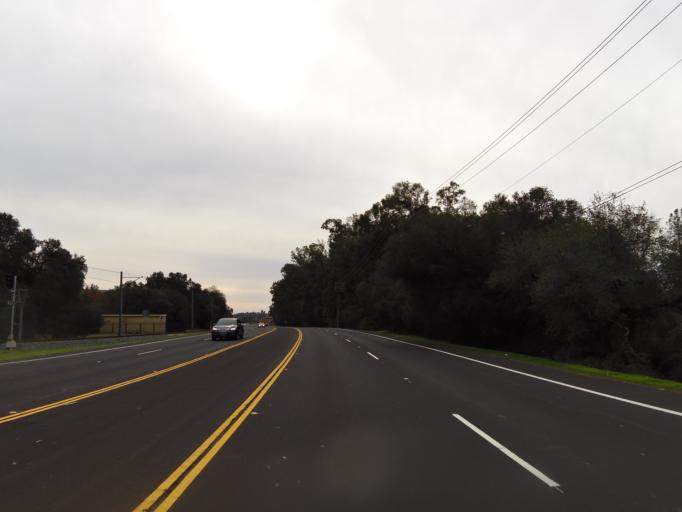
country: US
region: California
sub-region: Sacramento County
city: Folsom
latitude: 38.6629
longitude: -121.1839
